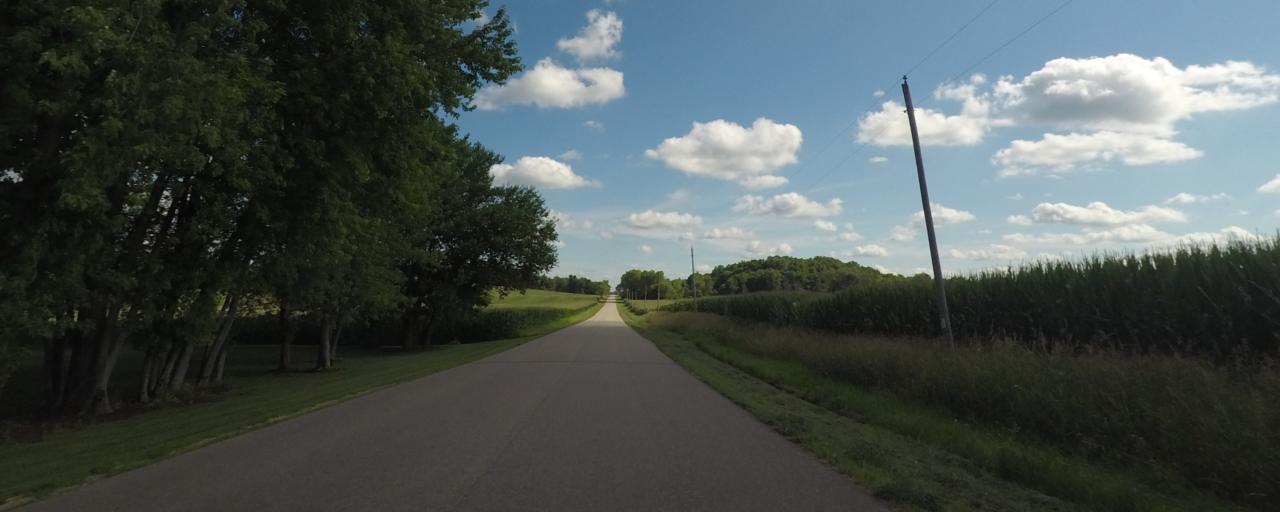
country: US
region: Wisconsin
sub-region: Dane County
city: Stoughton
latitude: 42.9090
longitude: -89.1319
